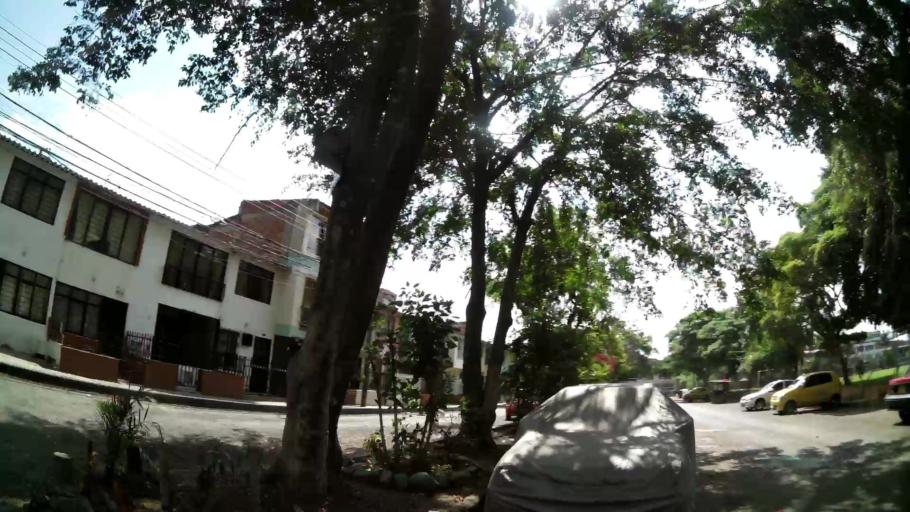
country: CO
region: Valle del Cauca
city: Cali
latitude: 3.4989
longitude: -76.4946
